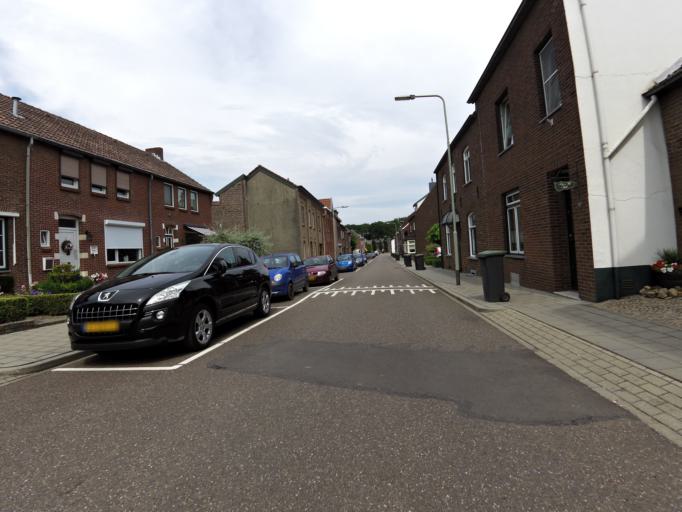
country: NL
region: Limburg
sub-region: Gemeente Simpelveld
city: Simpelveld
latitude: 50.8137
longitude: 6.0053
